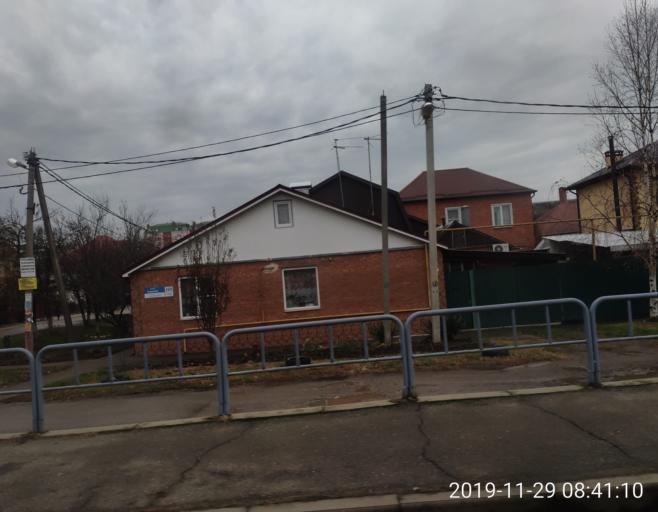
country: RU
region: Krasnodarskiy
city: Krasnodar
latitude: 45.0469
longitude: 38.9965
